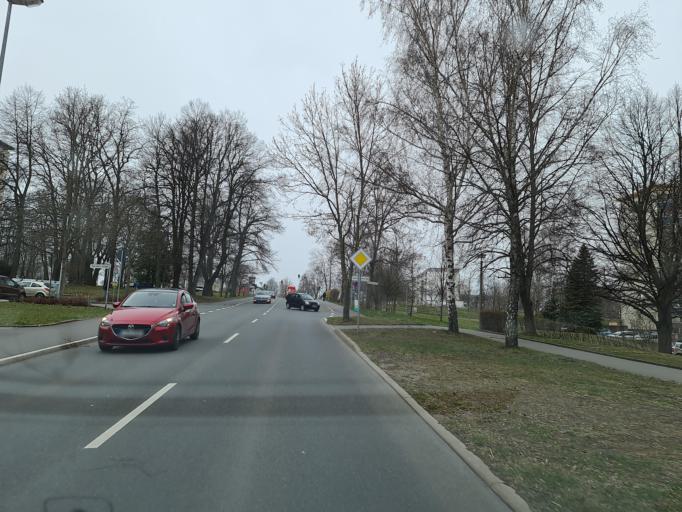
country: DE
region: Saxony
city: Neukirchen
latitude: 50.8043
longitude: 12.8903
